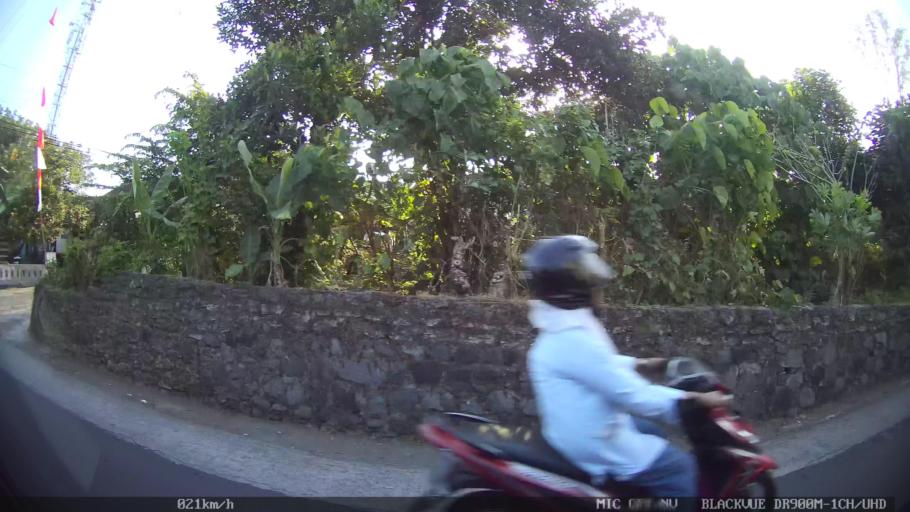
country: ID
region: Daerah Istimewa Yogyakarta
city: Gamping Lor
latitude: -7.7949
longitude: 110.3364
